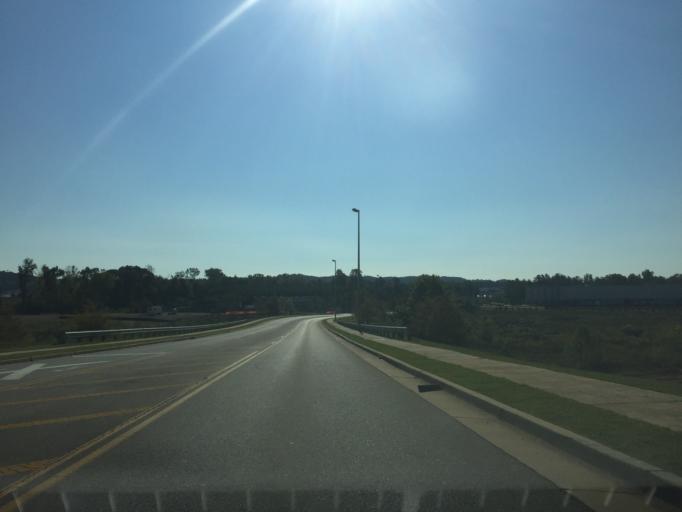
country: US
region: Tennessee
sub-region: Hamilton County
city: Harrison
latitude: 35.0747
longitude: -85.1477
